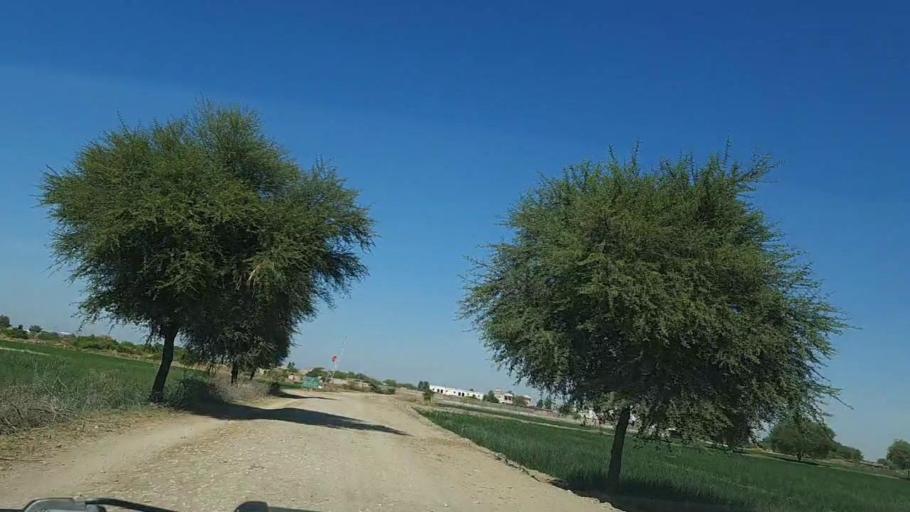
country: PK
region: Sindh
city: Dhoro Naro
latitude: 25.5288
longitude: 69.5039
